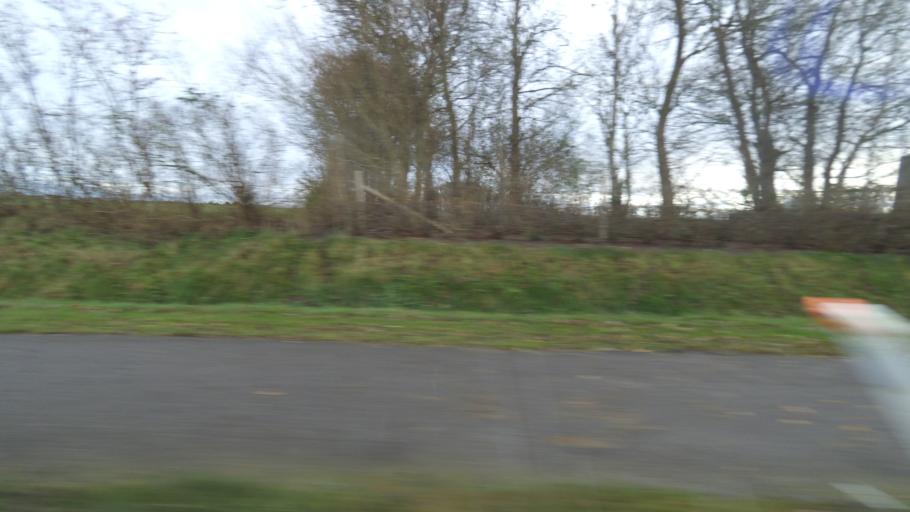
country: DK
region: Central Jutland
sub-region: Arhus Kommune
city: Malling
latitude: 56.0122
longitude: 10.2577
